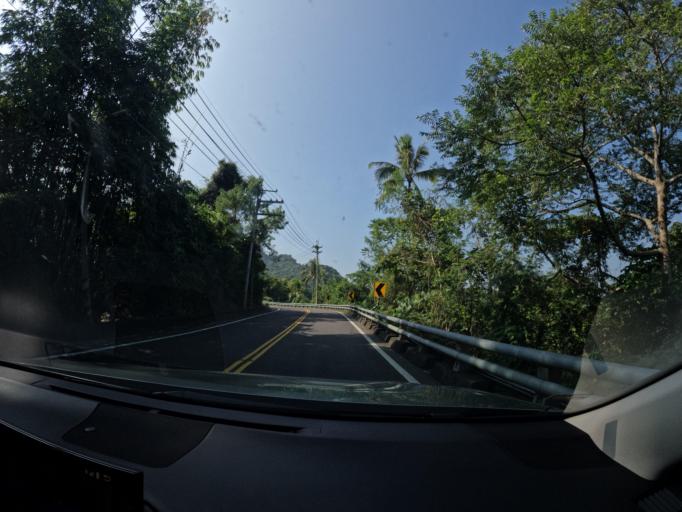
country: TW
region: Taiwan
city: Yujing
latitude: 23.0780
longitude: 120.6068
